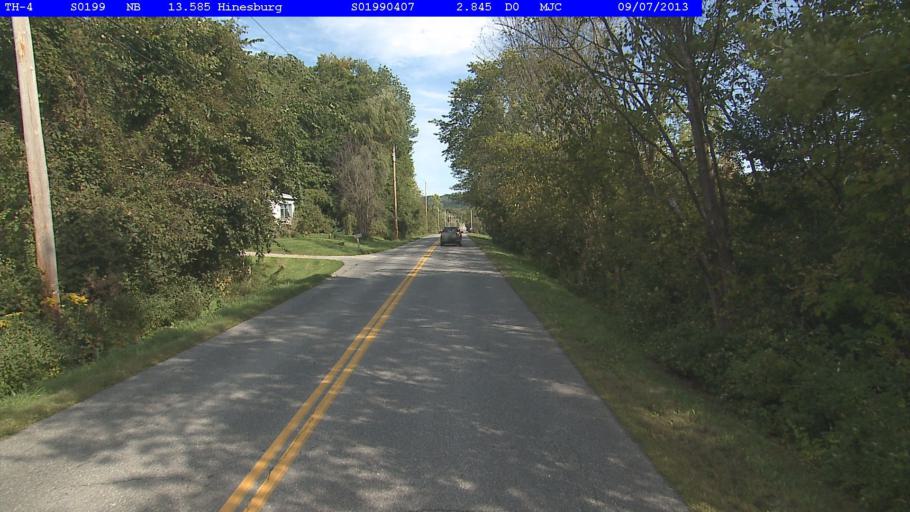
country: US
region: Vermont
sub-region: Chittenden County
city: Hinesburg
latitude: 44.3188
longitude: -73.1100
